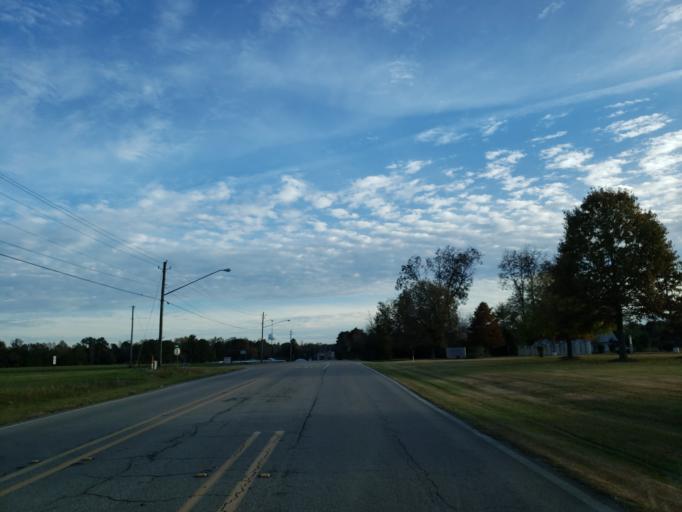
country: US
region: Mississippi
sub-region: Lamar County
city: Purvis
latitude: 31.1670
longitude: -89.4243
